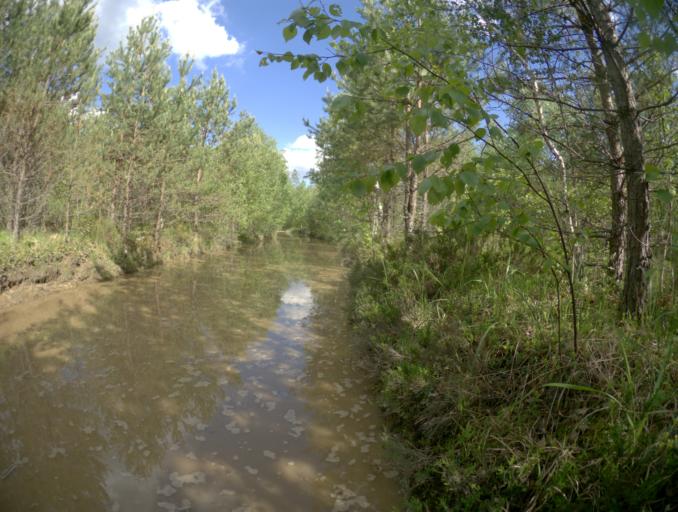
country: RU
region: Vladimir
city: Zolotkovo
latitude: 55.3299
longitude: 40.9639
